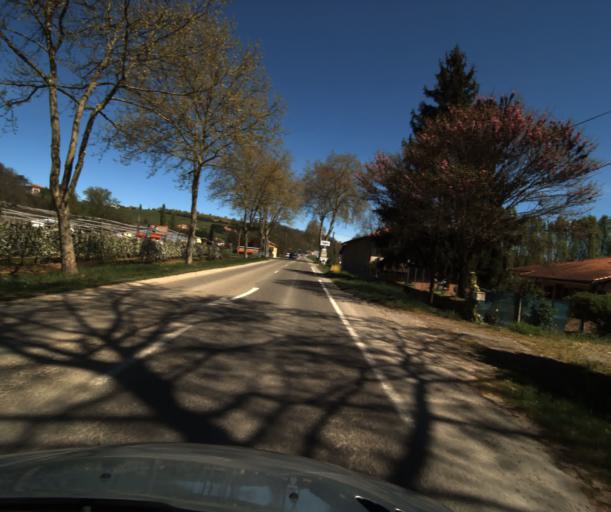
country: FR
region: Midi-Pyrenees
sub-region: Departement du Tarn-et-Garonne
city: Moissac
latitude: 44.1168
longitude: 1.1158
